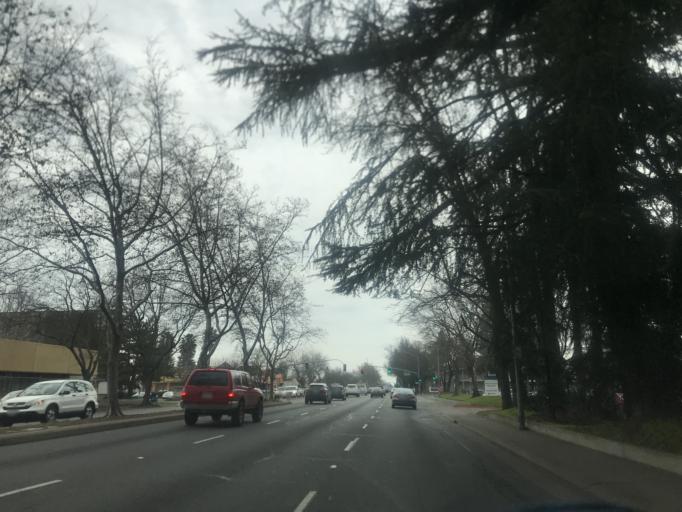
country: US
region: California
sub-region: Sacramento County
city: Arden-Arcade
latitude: 38.5804
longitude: -121.4153
